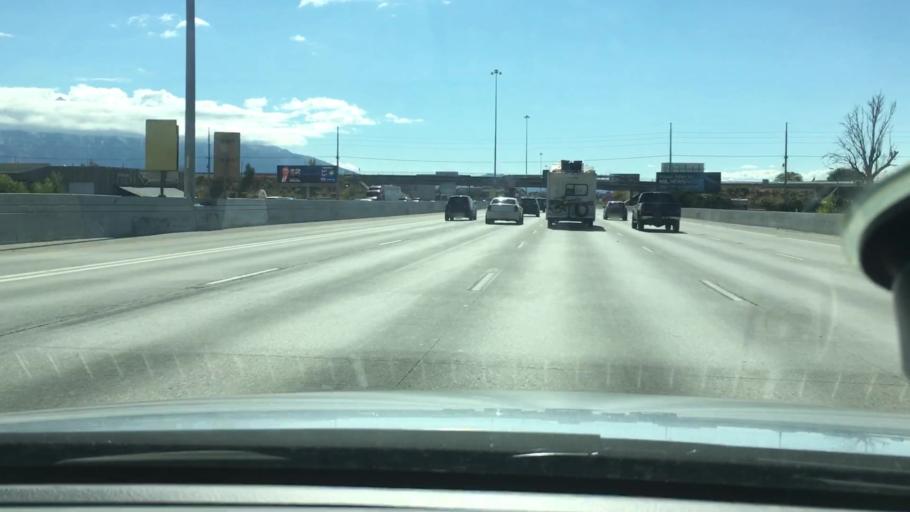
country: US
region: Utah
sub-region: Salt Lake County
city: Centerfield
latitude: 40.6889
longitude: -111.9037
